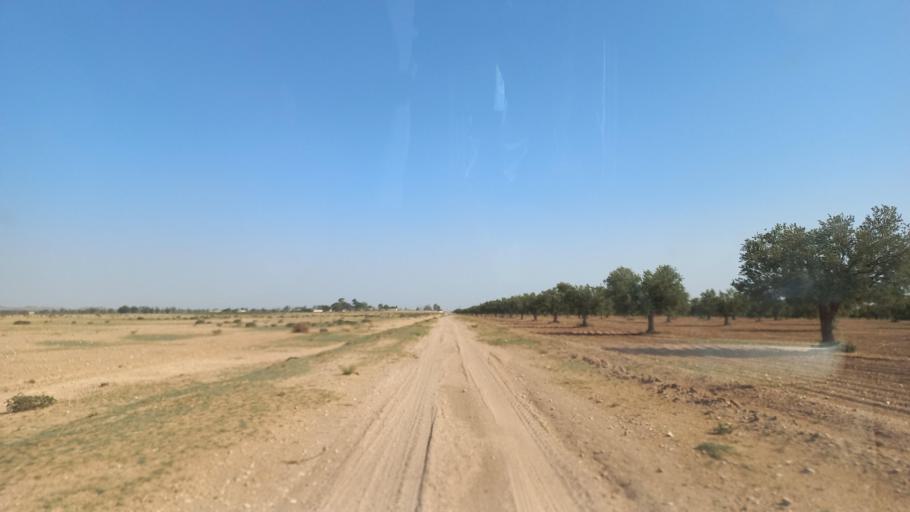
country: TN
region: Al Qasrayn
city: Kasserine
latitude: 35.3035
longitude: 9.0248
